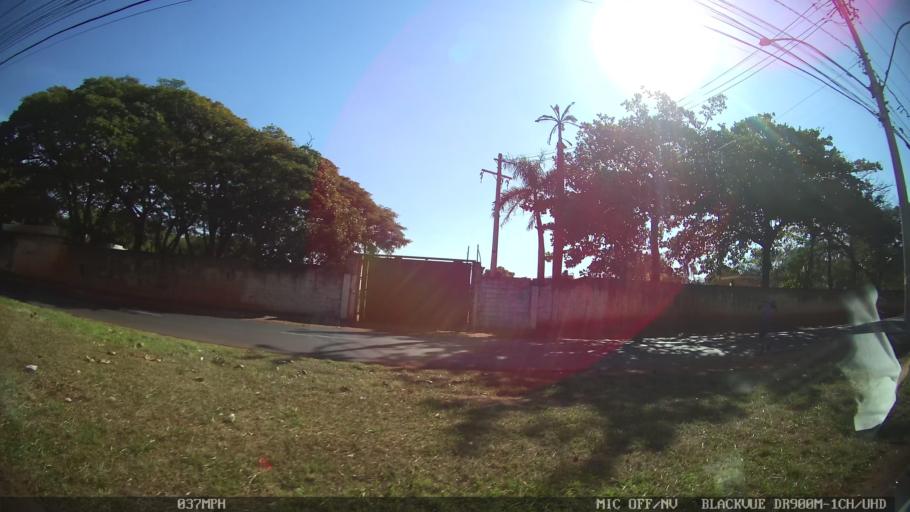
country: BR
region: Sao Paulo
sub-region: Ribeirao Preto
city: Ribeirao Preto
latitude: -21.1528
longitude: -47.7678
